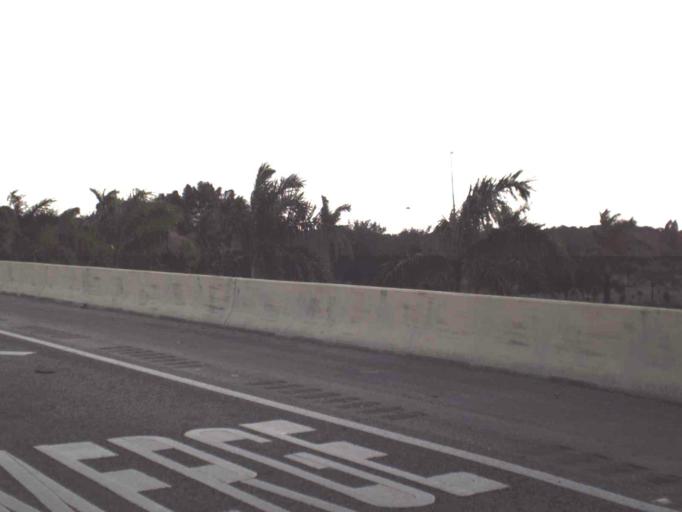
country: US
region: Florida
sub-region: Miami-Dade County
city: Scott Lake
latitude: 25.9552
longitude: -80.2293
